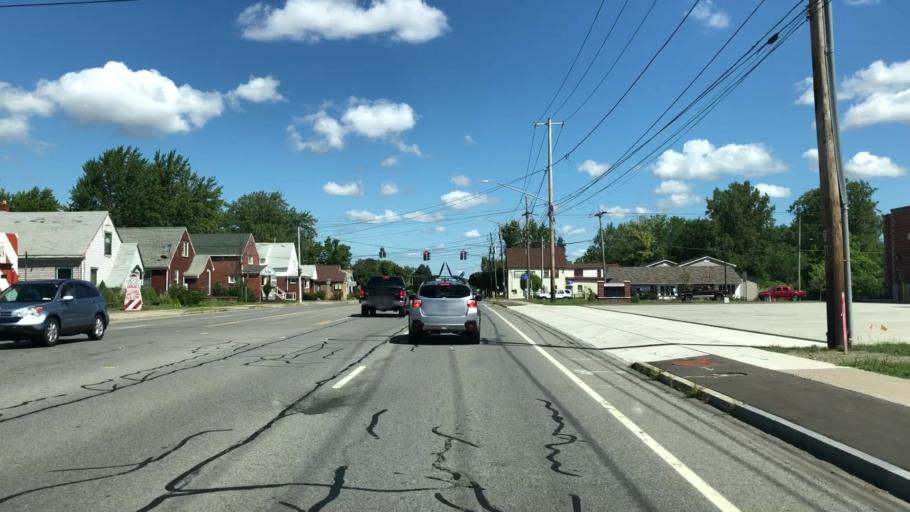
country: US
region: New York
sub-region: Erie County
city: West Seneca
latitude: 42.8503
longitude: -78.7545
